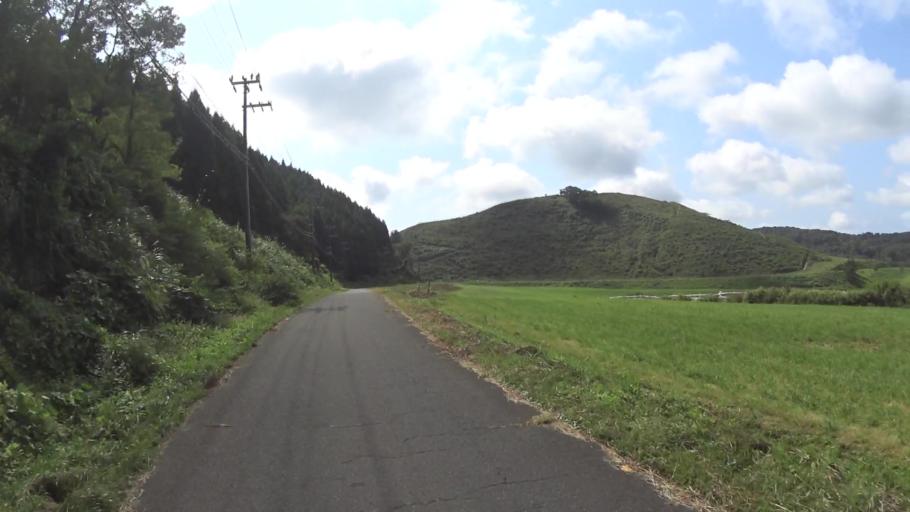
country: JP
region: Kyoto
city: Miyazu
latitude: 35.7263
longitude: 135.1981
